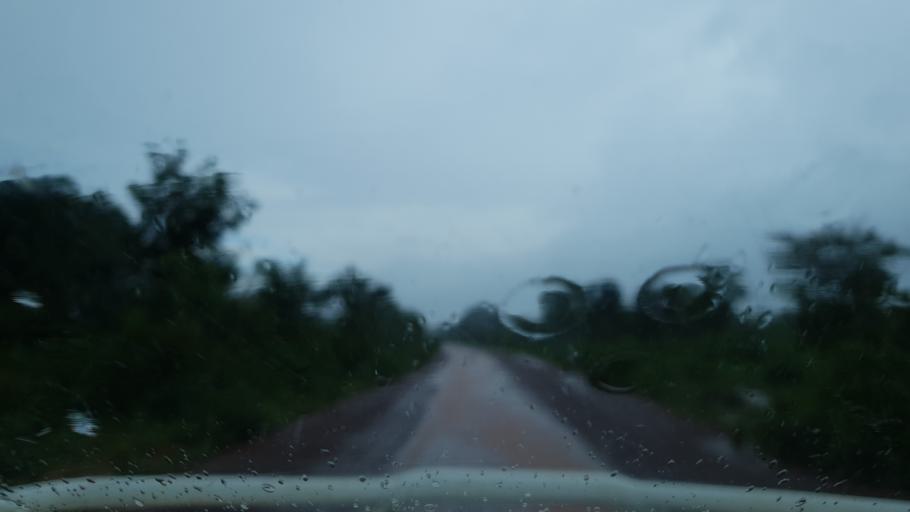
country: ML
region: Sikasso
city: Kolondieba
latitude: 11.6040
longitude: -6.6736
